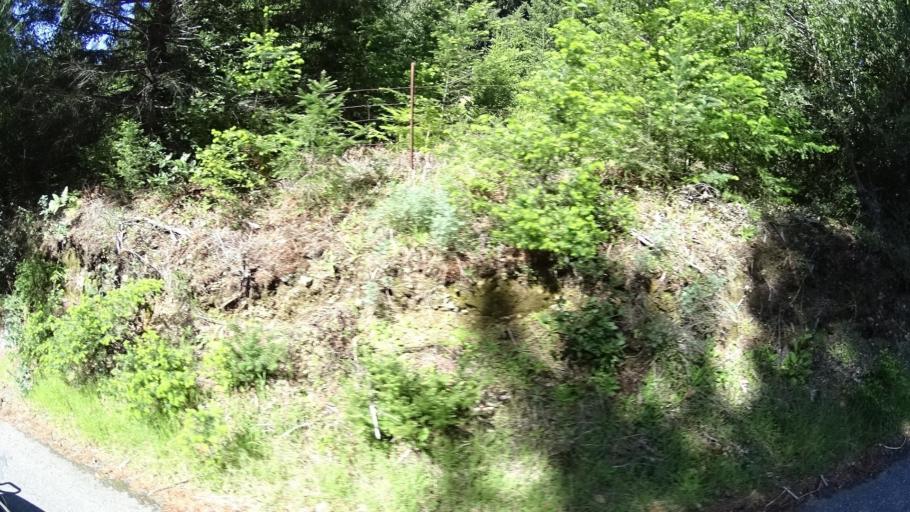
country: US
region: California
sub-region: Humboldt County
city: Redway
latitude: 40.1840
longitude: -124.0900
